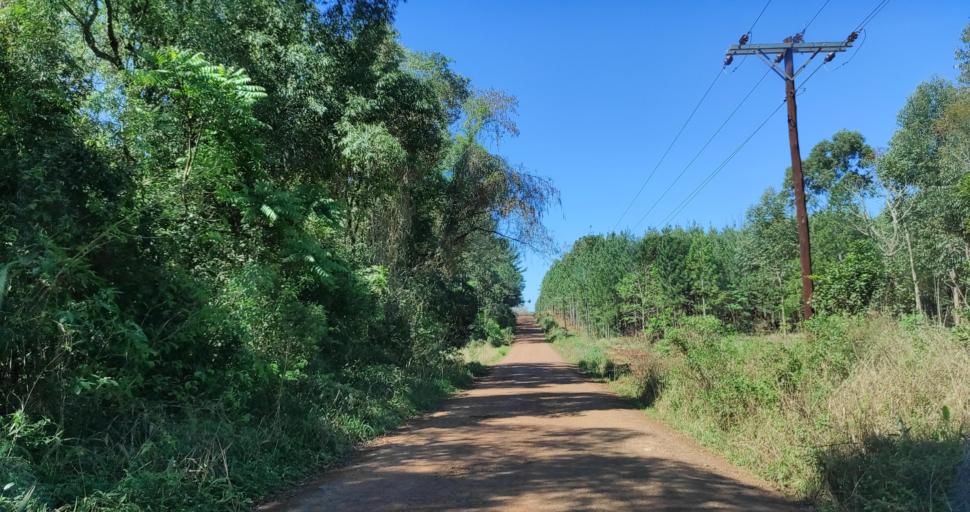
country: AR
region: Misiones
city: Capiovi
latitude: -26.9351
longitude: -55.0279
